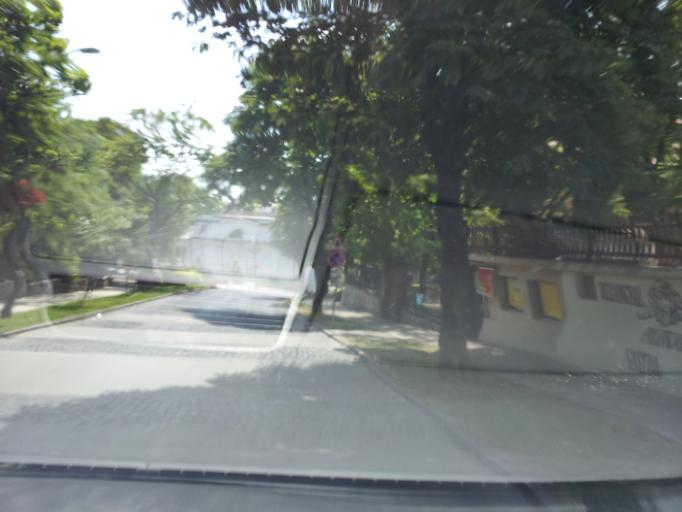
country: HU
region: Veszprem
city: Balatonfured
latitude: 46.9553
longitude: 17.8916
